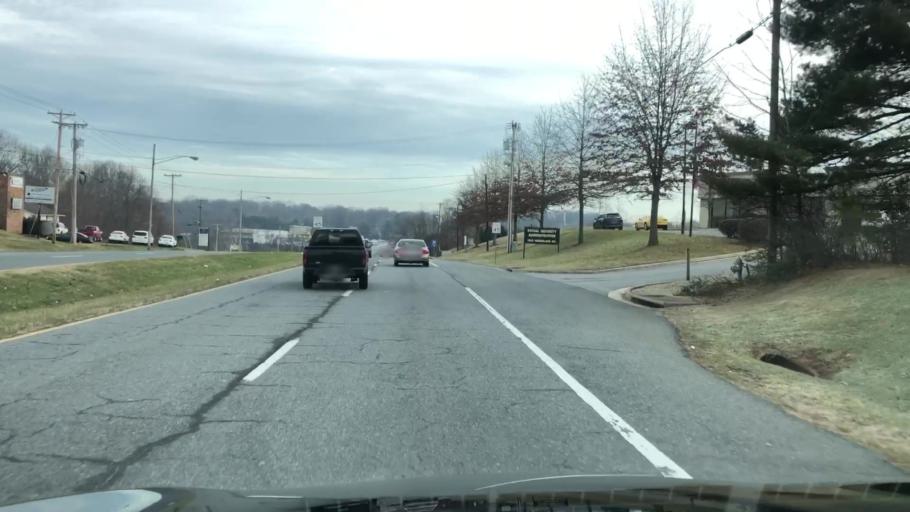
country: US
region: Virginia
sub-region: Campbell County
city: Timberlake
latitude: 37.3548
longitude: -79.2225
